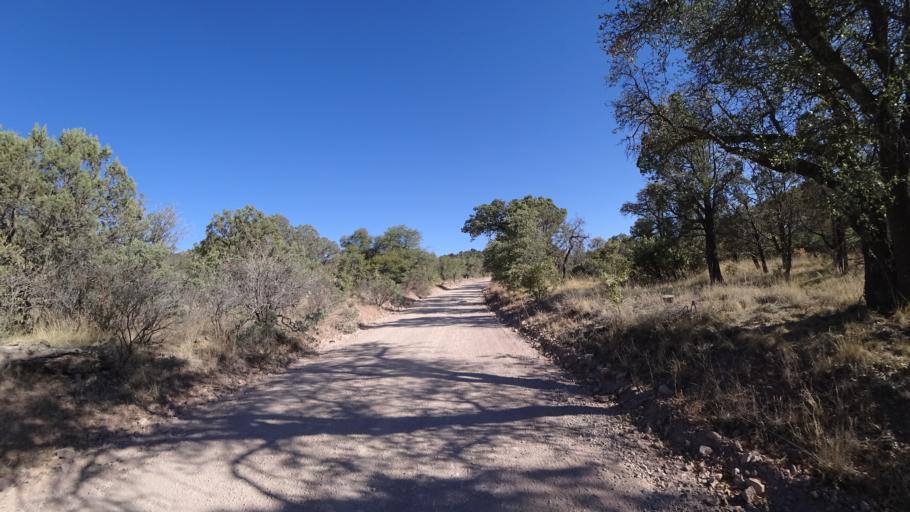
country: US
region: Arizona
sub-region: Cochise County
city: Huachuca City
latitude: 31.5045
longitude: -110.5582
